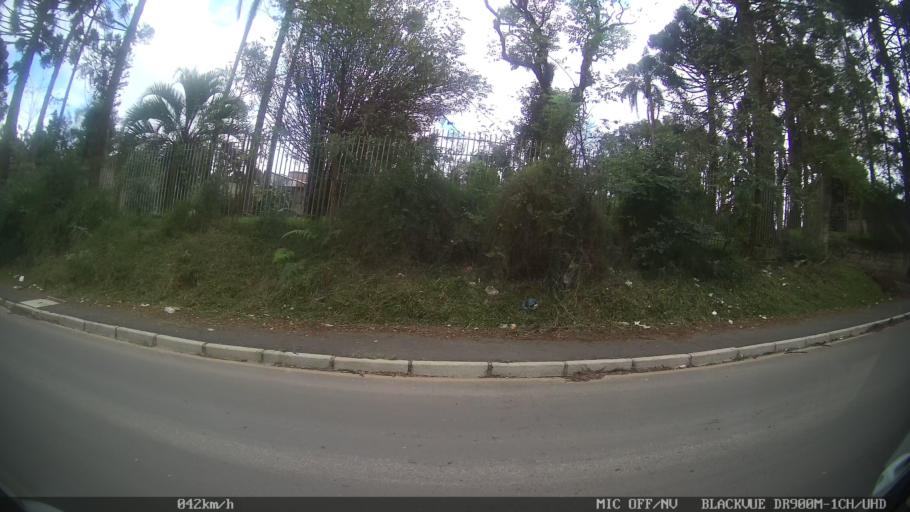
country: BR
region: Parana
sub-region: Colombo
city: Colombo
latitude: -25.3485
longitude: -49.2263
